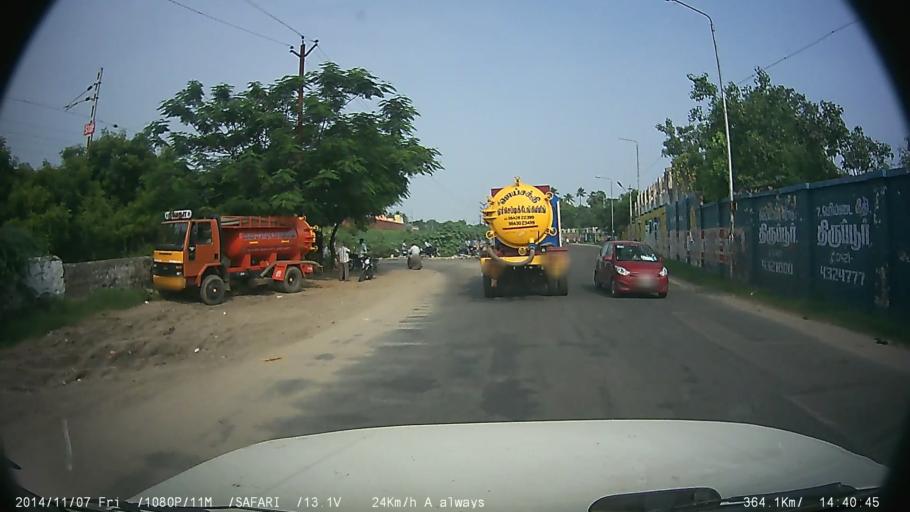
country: IN
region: Tamil Nadu
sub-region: Tiruppur
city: Tiruppur
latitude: 11.1115
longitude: 77.3517
